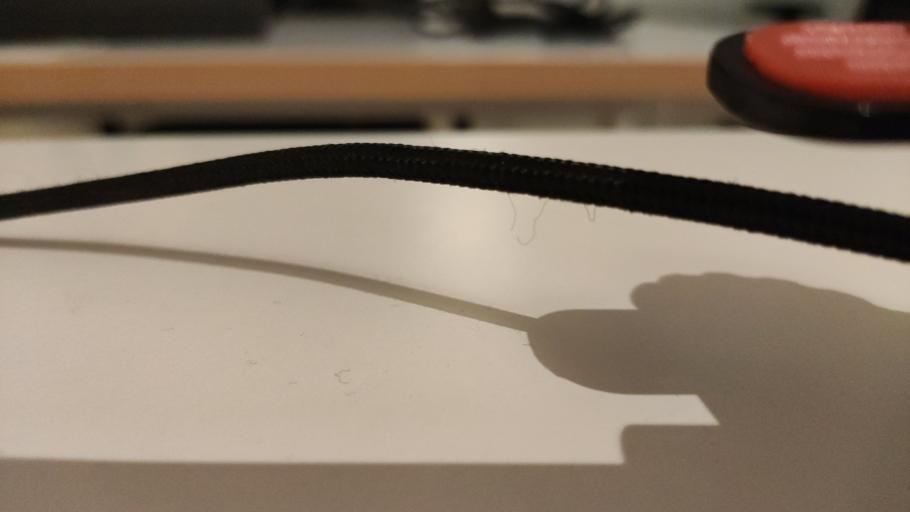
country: RU
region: Moskovskaya
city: Malino
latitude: 55.1078
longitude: 38.1068
